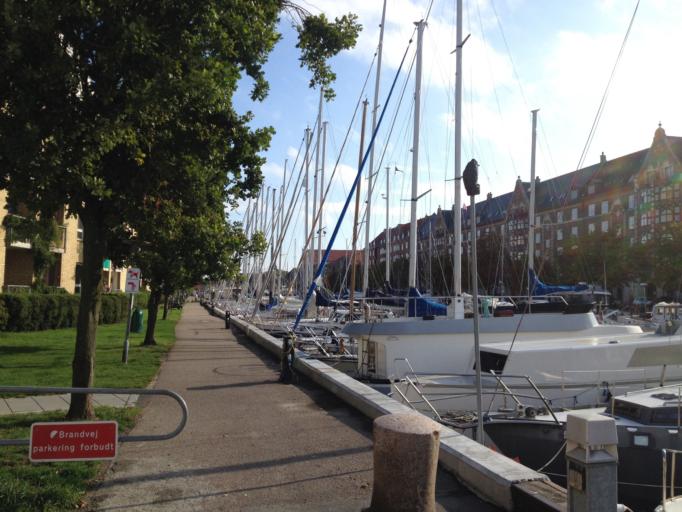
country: DK
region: Capital Region
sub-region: Kobenhavn
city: Christianshavn
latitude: 55.6754
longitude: 12.5951
